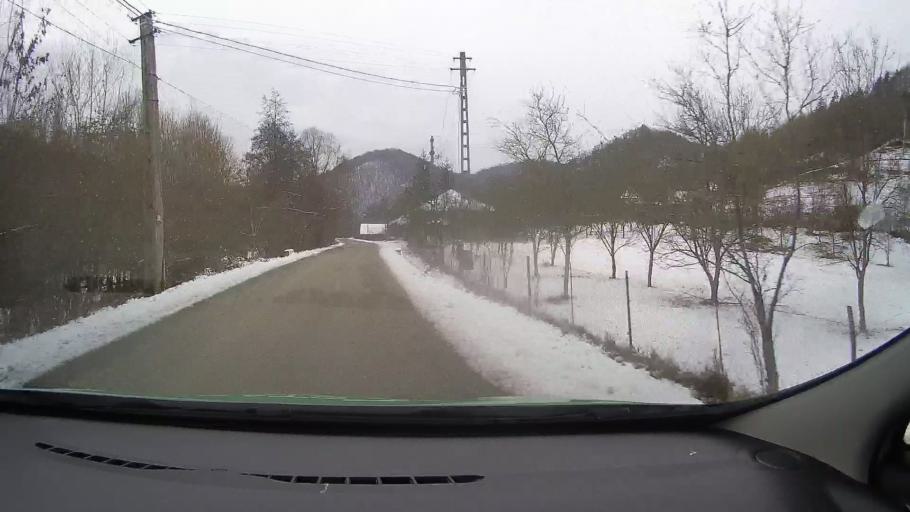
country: RO
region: Hunedoara
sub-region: Comuna Balsa
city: Balsa
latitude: 46.0546
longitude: 23.0786
